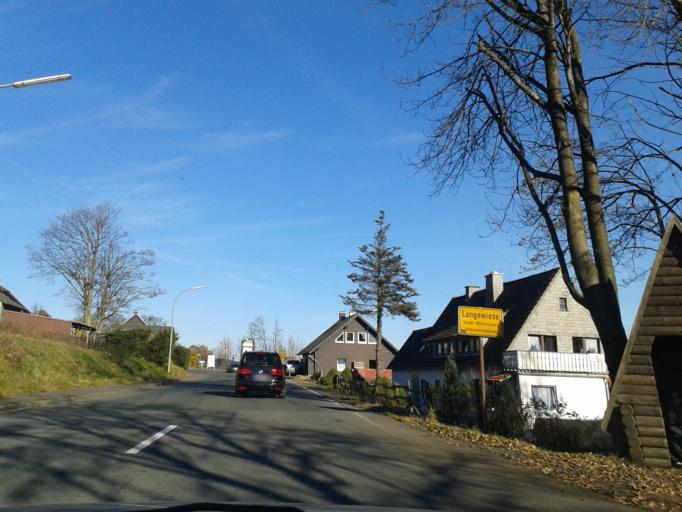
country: DE
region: North Rhine-Westphalia
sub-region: Regierungsbezirk Arnsberg
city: Winterberg
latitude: 51.1500
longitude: 8.4617
